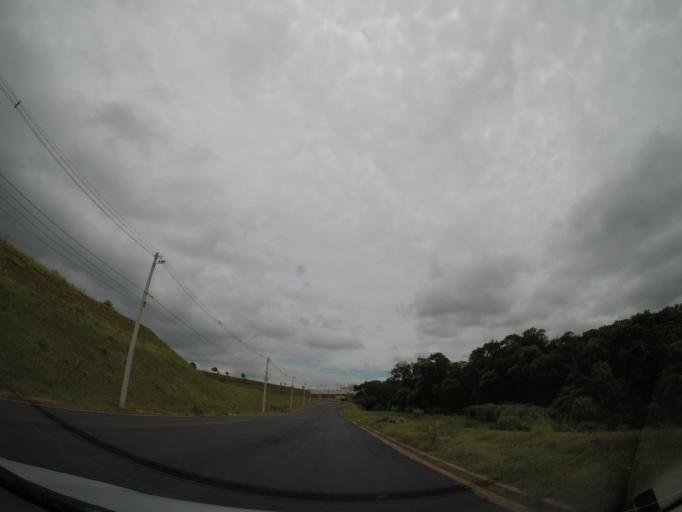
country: BR
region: Sao Paulo
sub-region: Vinhedo
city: Vinhedo
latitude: -23.0746
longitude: -47.0102
